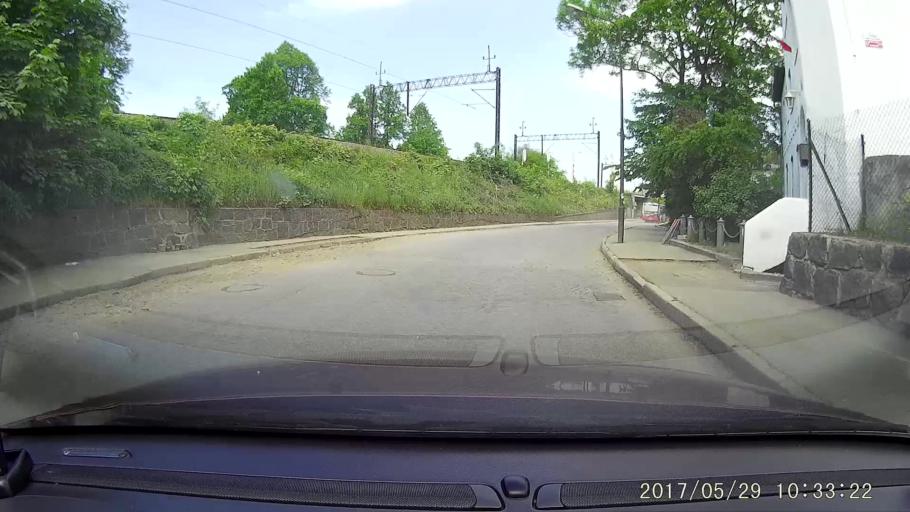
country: PL
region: Lower Silesian Voivodeship
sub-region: Jelenia Gora
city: Jelenia Gora
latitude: 50.9056
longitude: 15.7464
